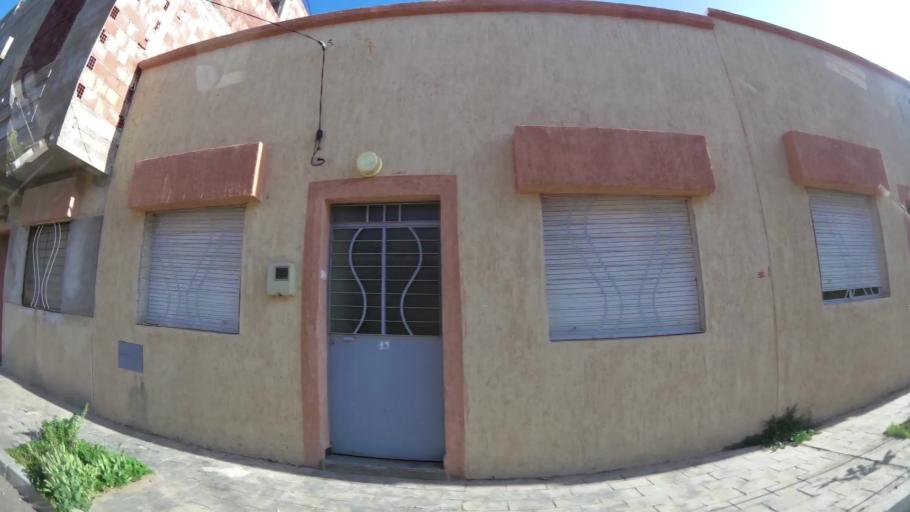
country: MA
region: Oriental
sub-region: Oujda-Angad
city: Oujda
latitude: 34.7151
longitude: -1.9051
